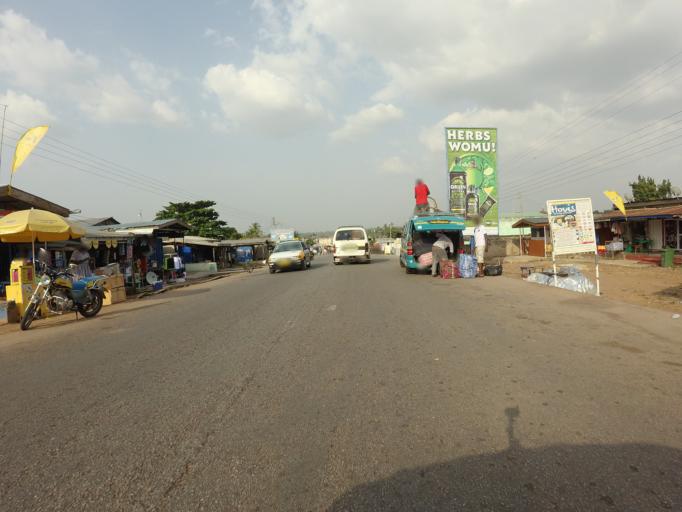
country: GH
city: Akropong
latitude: 6.2521
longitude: 0.1322
